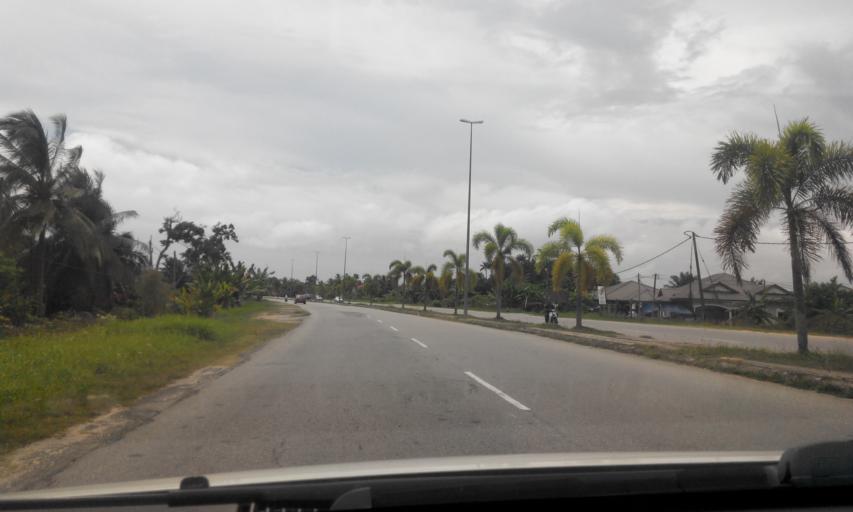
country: MY
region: Perak
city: Parit Buntar
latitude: 5.1270
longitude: 100.5124
